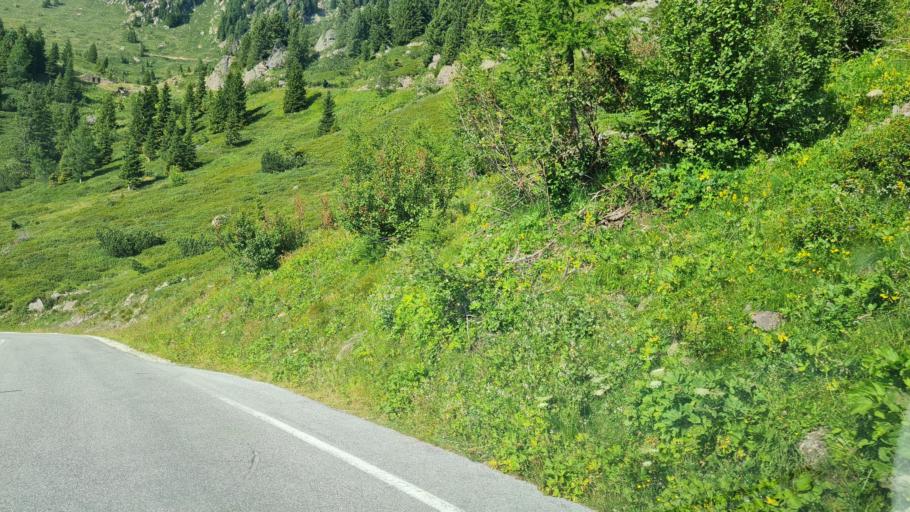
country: IT
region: Trentino-Alto Adige
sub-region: Provincia di Trento
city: Torcegno
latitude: 46.1691
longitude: 11.4431
